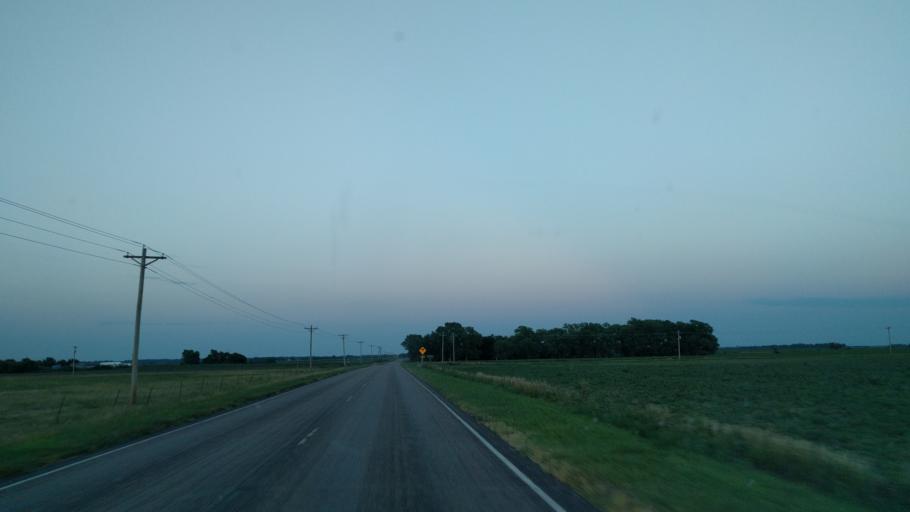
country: US
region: Kansas
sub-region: Reno County
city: Nickerson
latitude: 38.2176
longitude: -98.1088
